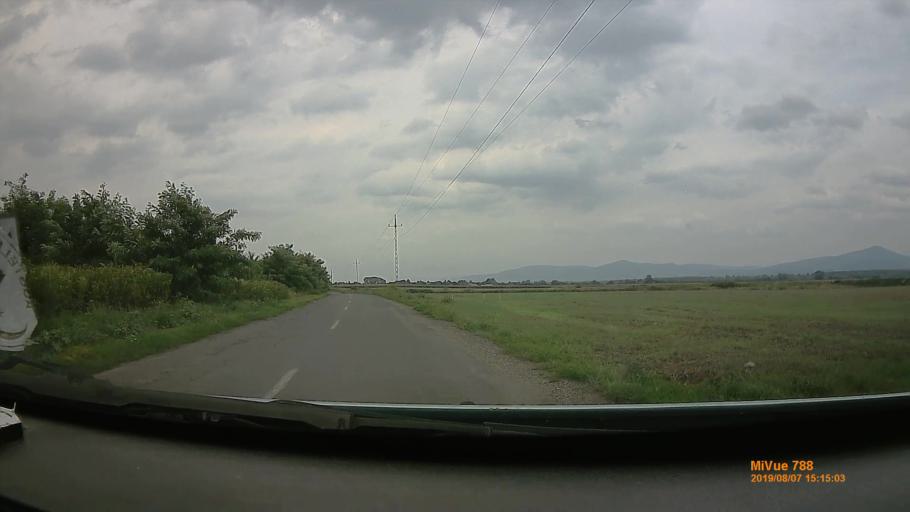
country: HU
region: Borsod-Abauj-Zemplen
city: Encs
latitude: 48.3354
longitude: 21.1270
